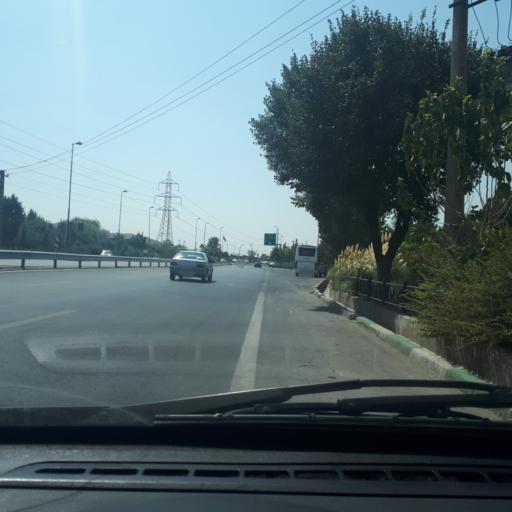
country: IR
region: Tehran
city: Tehran
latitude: 35.7039
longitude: 51.5072
